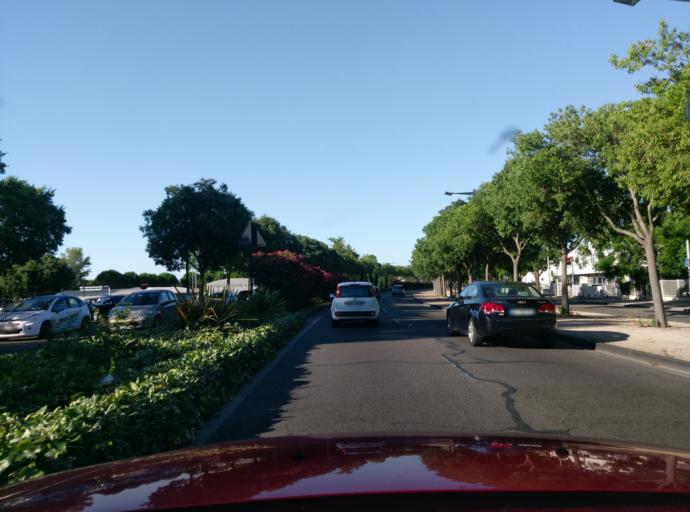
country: FR
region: Languedoc-Roussillon
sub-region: Departement du Gard
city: Nimes
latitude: 43.8360
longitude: 4.3880
